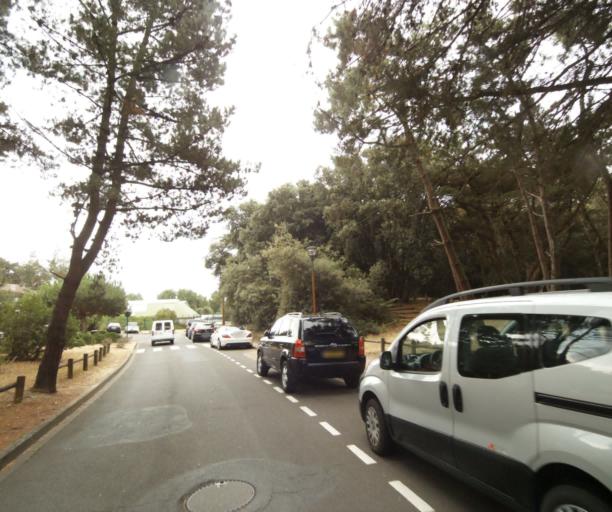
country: FR
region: Pays de la Loire
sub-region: Departement de la Vendee
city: Chateau-d'Olonne
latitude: 46.4849
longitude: -1.7592
